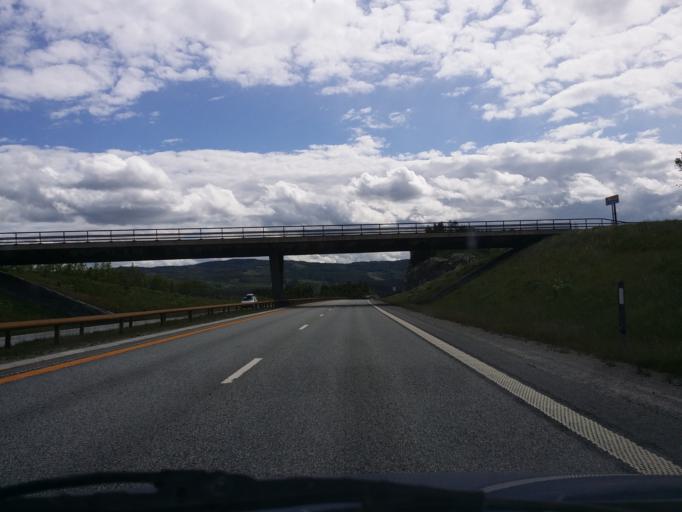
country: NO
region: Hedmark
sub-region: Stange
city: Stange
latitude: 60.6338
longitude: 11.2993
